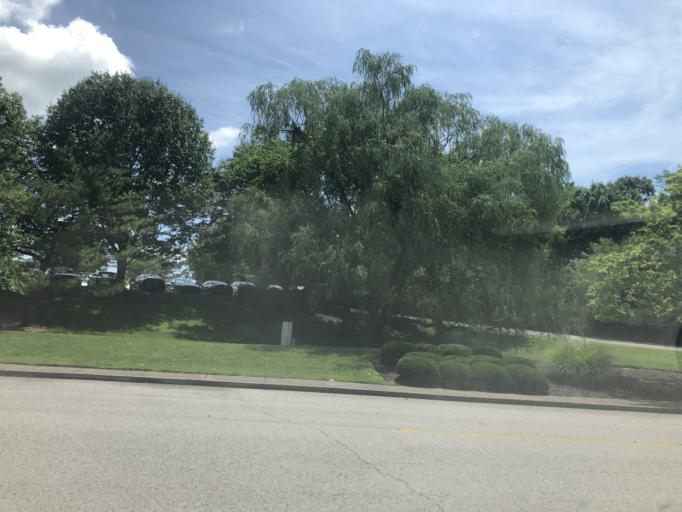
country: US
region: Tennessee
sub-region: Davidson County
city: Lakewood
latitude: 36.2531
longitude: -86.6823
